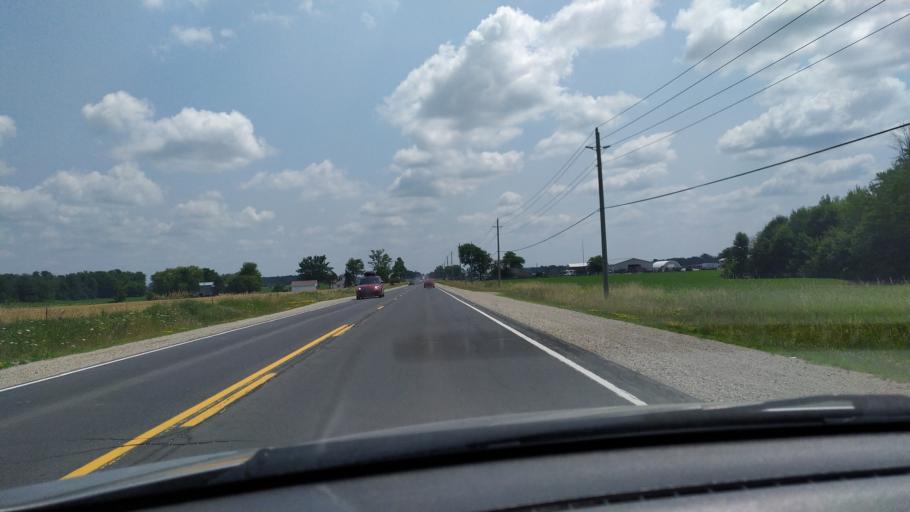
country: CA
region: Ontario
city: Stratford
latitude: 43.3702
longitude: -80.9060
